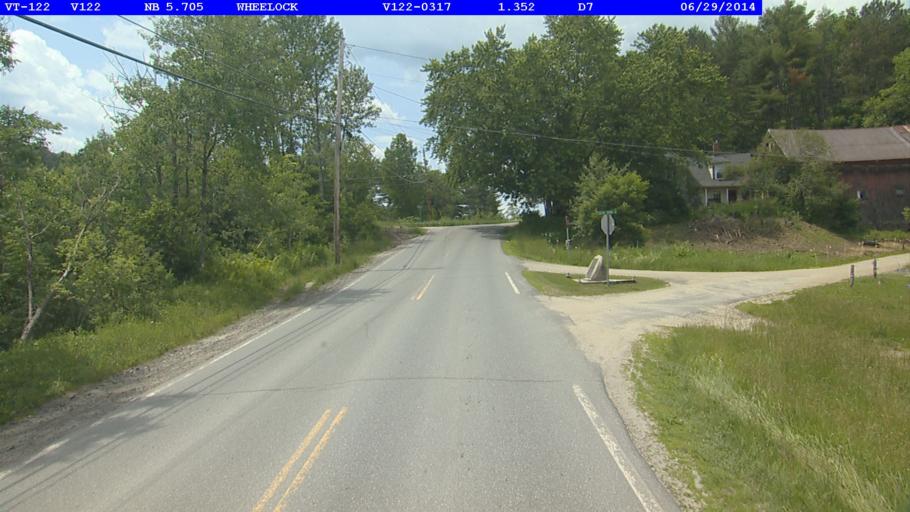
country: US
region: Vermont
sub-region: Caledonia County
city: Lyndonville
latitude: 44.5886
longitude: -72.0881
